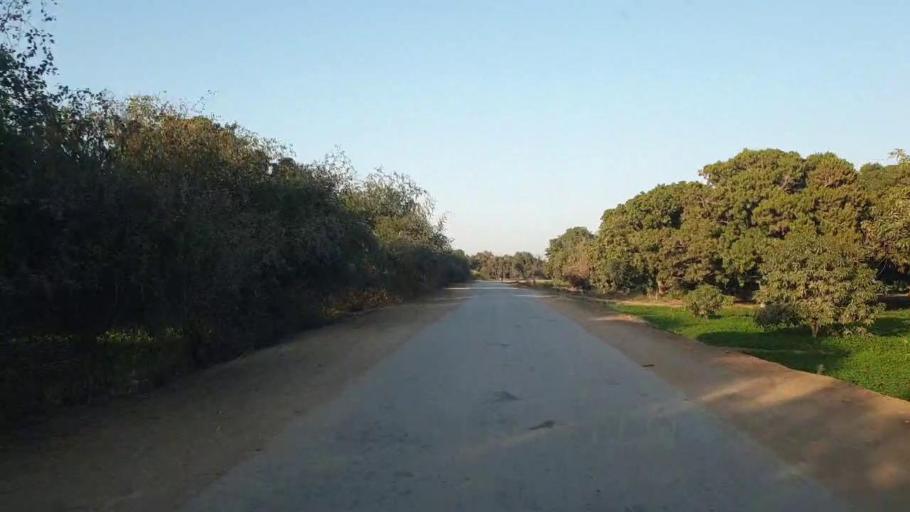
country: PK
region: Sindh
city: Tando Allahyar
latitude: 25.3918
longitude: 68.7604
